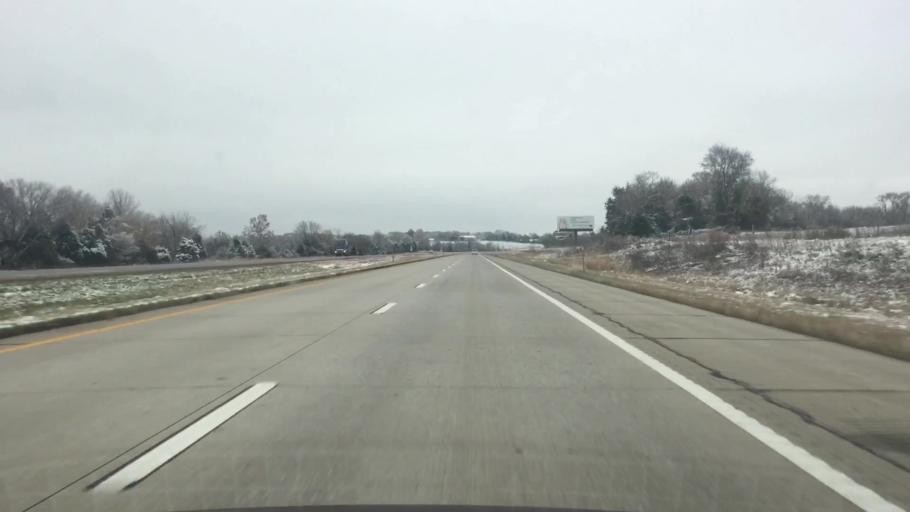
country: US
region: Missouri
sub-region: Saint Clair County
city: Osceola
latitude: 38.1807
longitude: -93.7282
